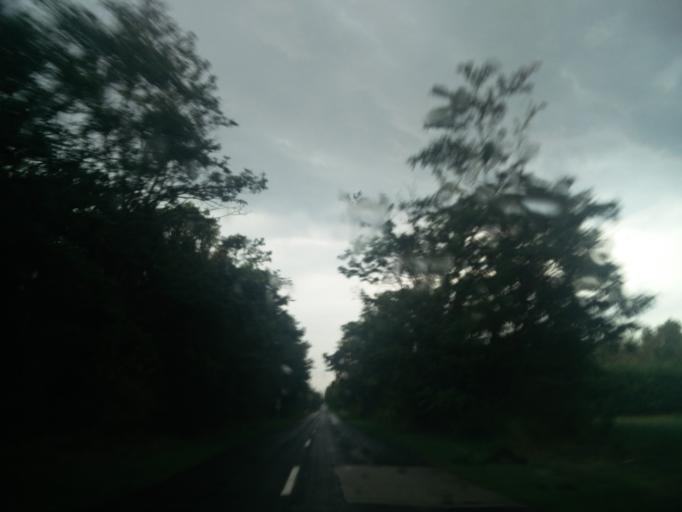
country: HU
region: Fejer
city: Lovasbereny
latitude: 47.2852
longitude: 18.5777
